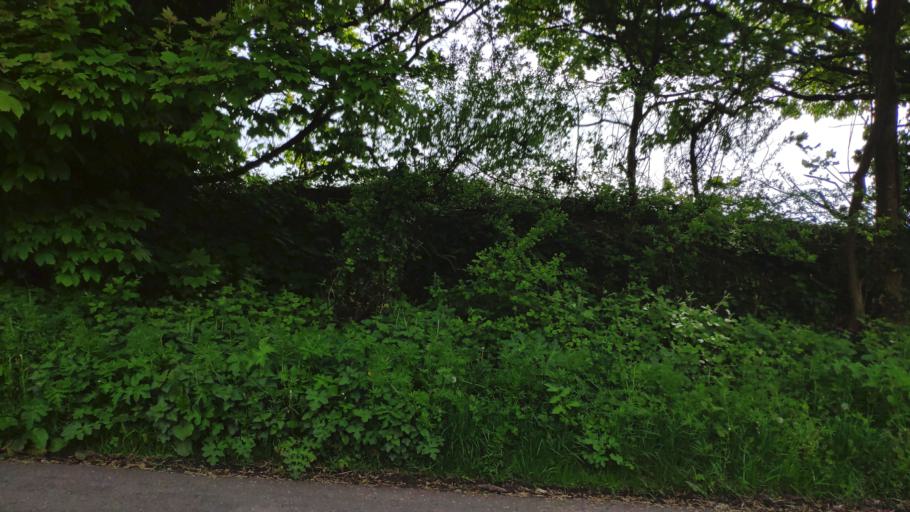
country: IE
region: Munster
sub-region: County Cork
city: Blarney
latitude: 51.9720
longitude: -8.5133
